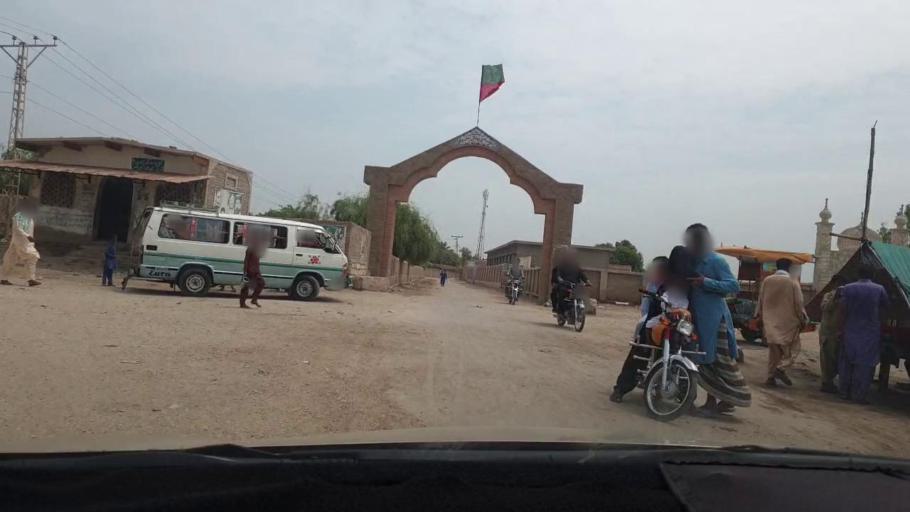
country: PK
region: Sindh
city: Ratodero
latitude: 27.7554
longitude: 68.3286
